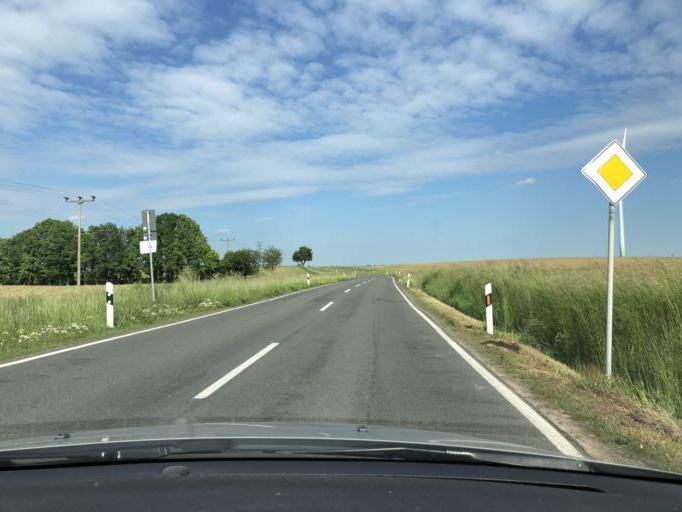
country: DE
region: Saxony
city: Nerchau
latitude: 51.2273
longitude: 12.8000
